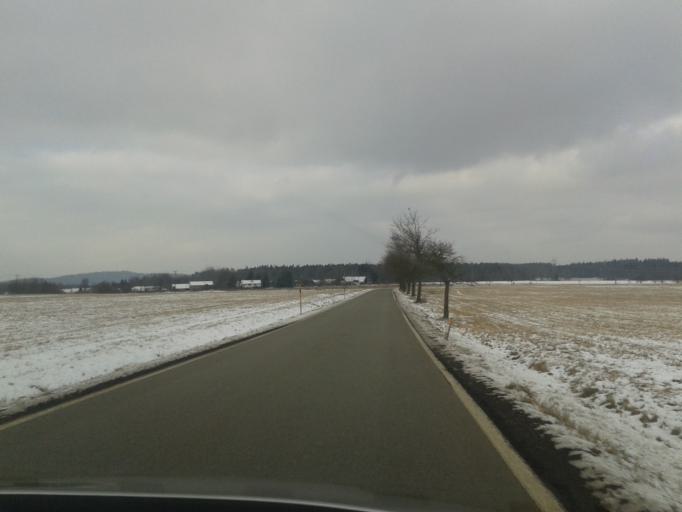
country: CZ
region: Olomoucky
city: Horni Stepanov
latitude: 49.5821
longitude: 16.8308
